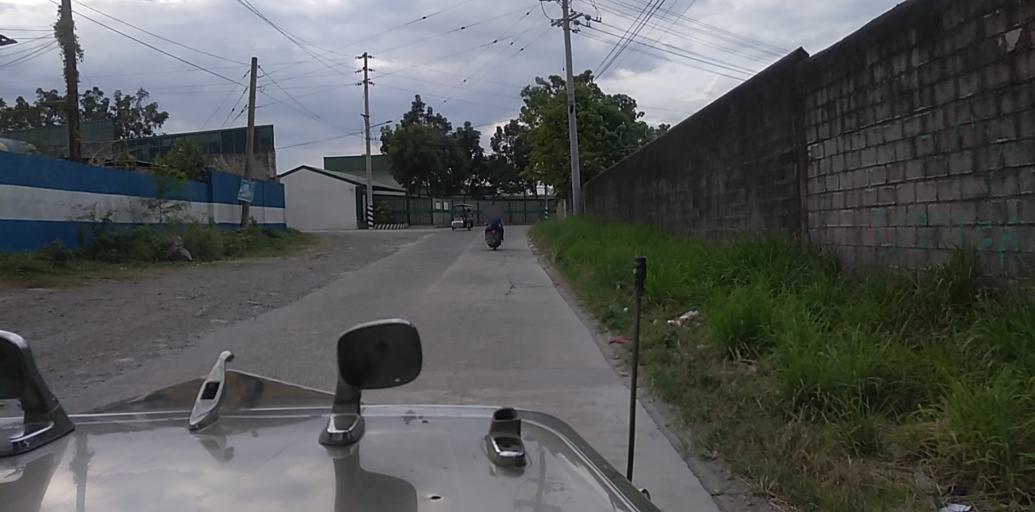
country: PH
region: Central Luzon
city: Santol
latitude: 15.1613
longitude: 120.5490
